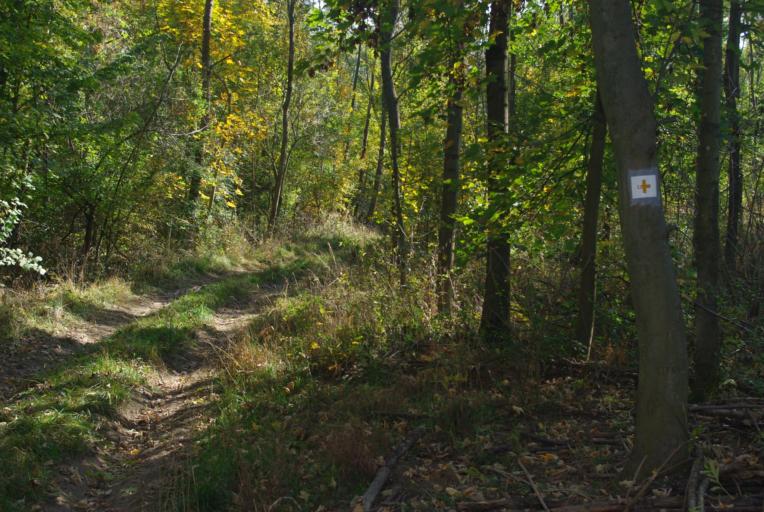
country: HU
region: Pest
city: Budakeszi
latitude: 47.5404
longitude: 18.8984
